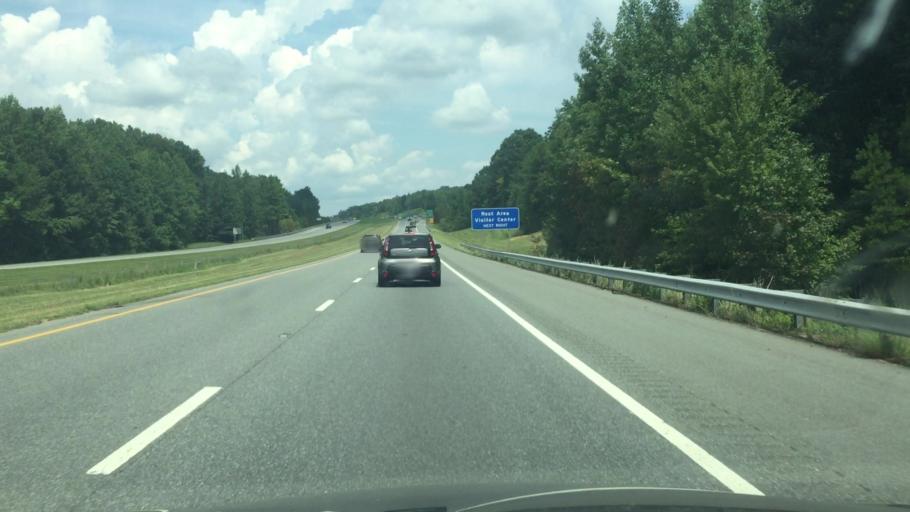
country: US
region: North Carolina
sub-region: Montgomery County
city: Biscoe
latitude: 35.5076
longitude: -79.7811
